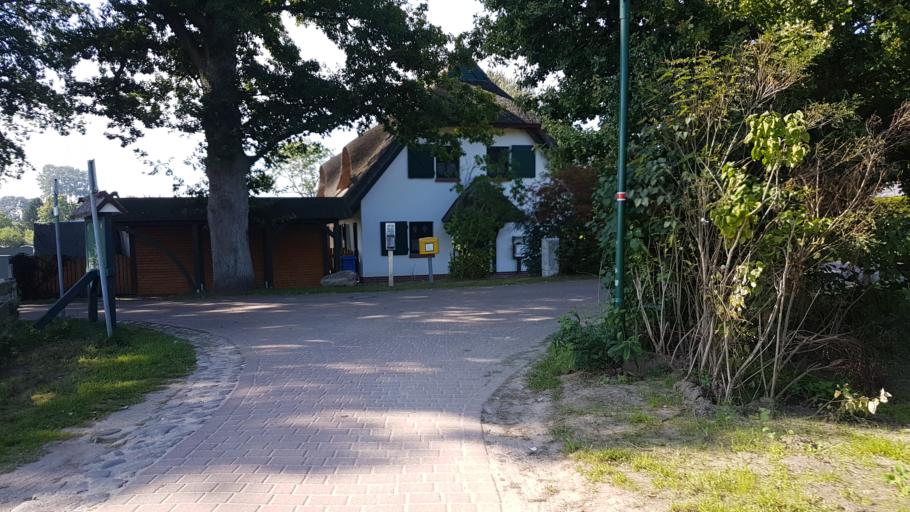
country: DE
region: Mecklenburg-Vorpommern
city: Ostseebad Binz
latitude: 54.3540
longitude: 13.5744
